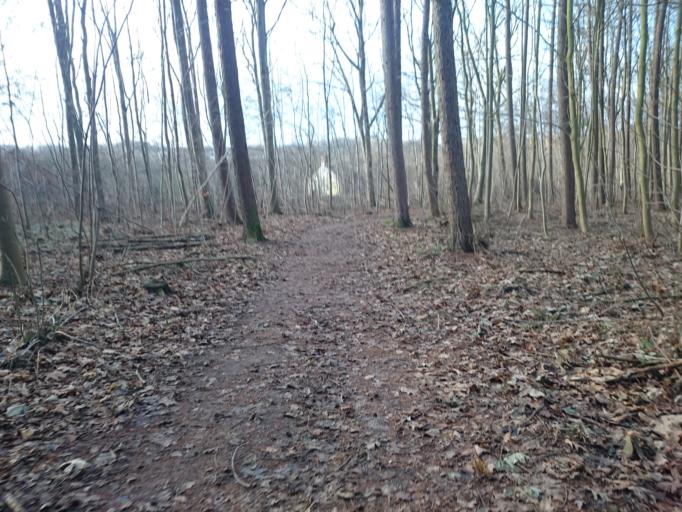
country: DK
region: Central Jutland
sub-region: Arhus Kommune
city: Stavtrup
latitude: 56.1294
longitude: 10.1403
